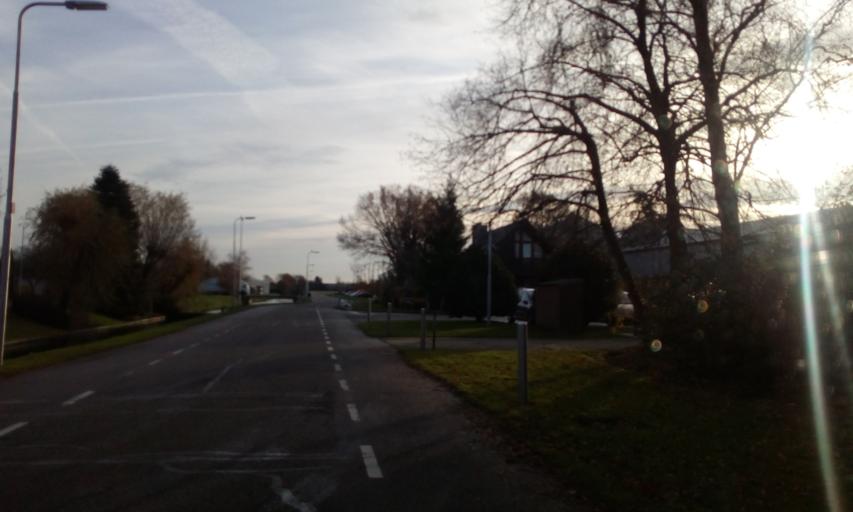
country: NL
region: South Holland
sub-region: Gemeente Lansingerland
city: Bleiswijk
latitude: 52.0041
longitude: 4.5181
